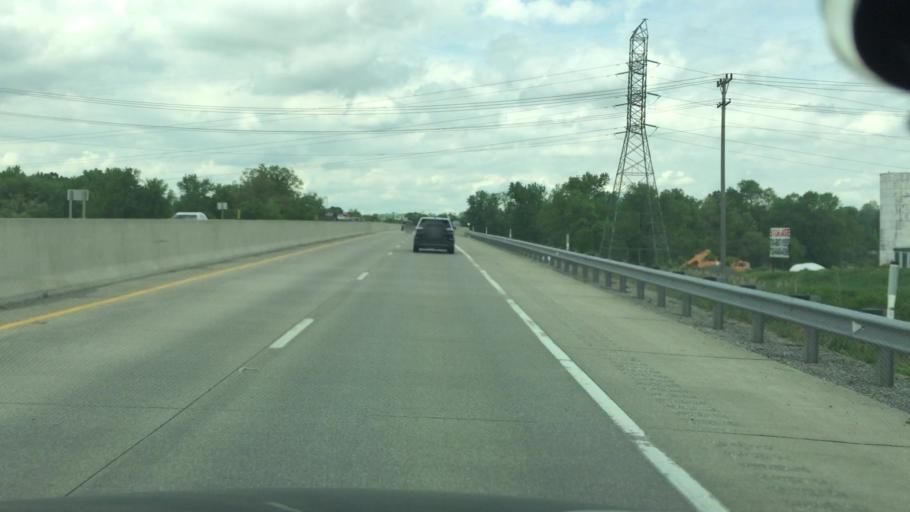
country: US
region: Pennsylvania
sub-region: Westmoreland County
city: Scottdale
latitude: 40.1106
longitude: -79.5550
